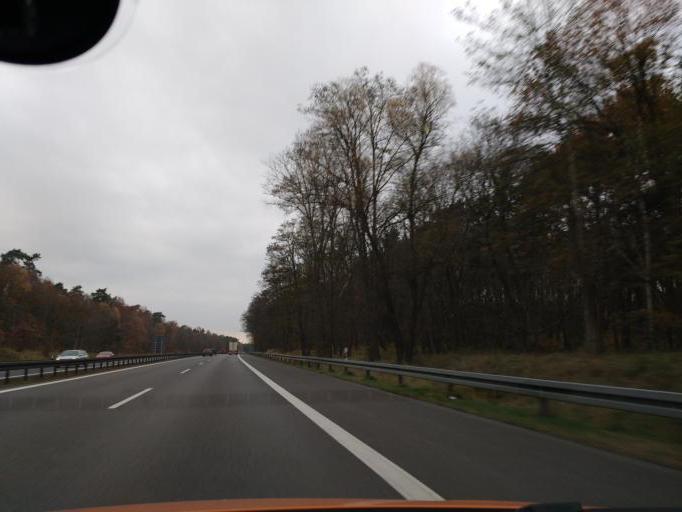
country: DE
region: Brandenburg
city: Fehrbellin
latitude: 52.7584
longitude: 12.8388
